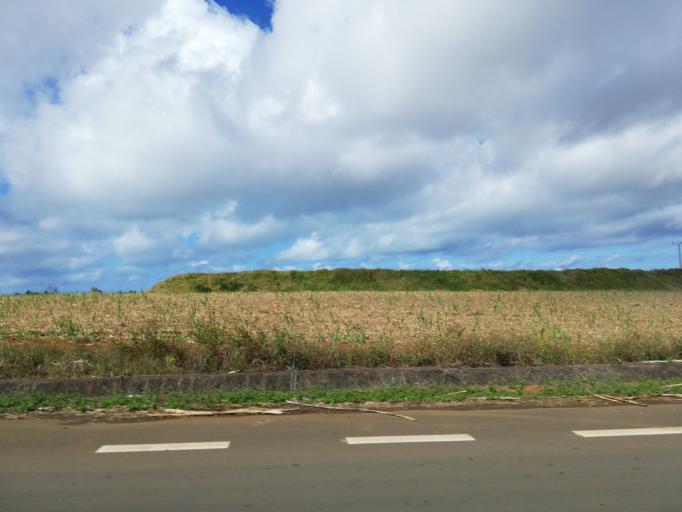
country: MU
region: Grand Port
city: Plaine Magnien
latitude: -20.4108
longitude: 57.6737
